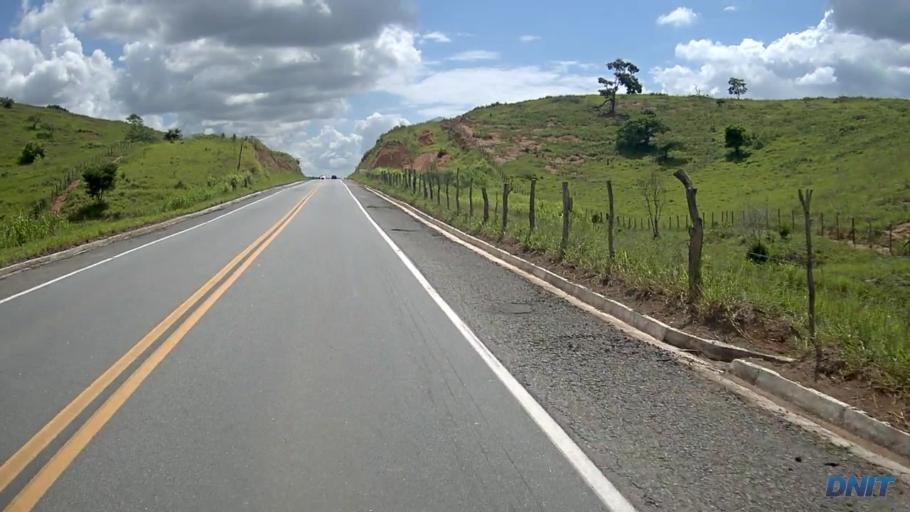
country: BR
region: Minas Gerais
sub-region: Governador Valadares
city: Governador Valadares
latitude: -18.9914
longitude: -42.1149
